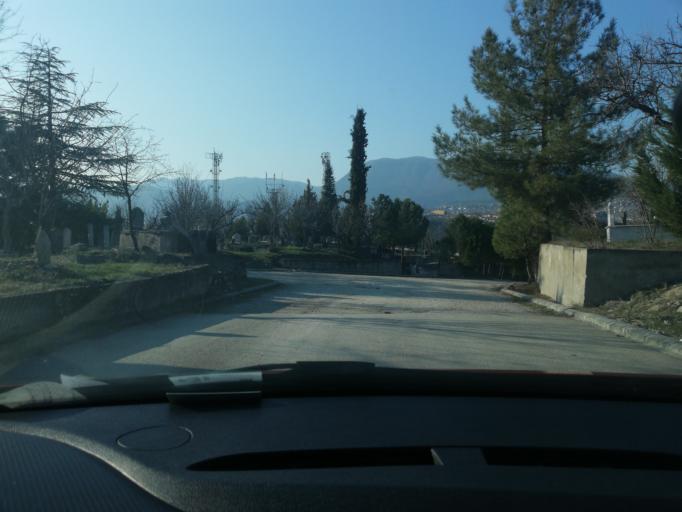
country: TR
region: Karabuk
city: Safranbolu
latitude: 41.2399
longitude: 32.6929
